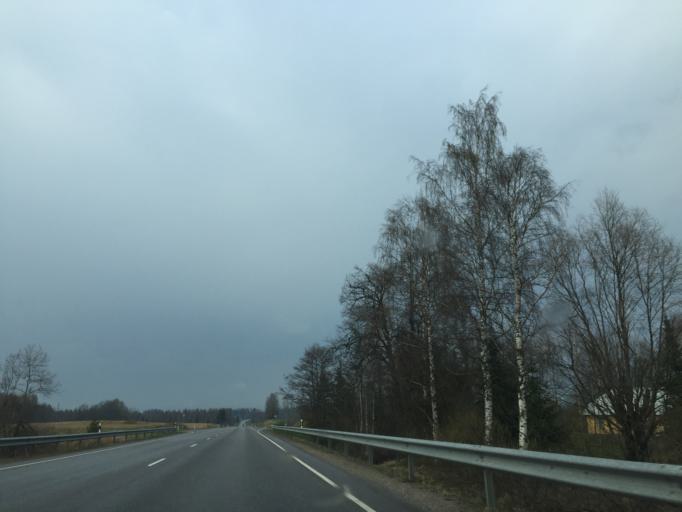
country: EE
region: Tartu
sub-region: UElenurme vald
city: Ulenurme
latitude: 58.1592
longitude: 26.6931
